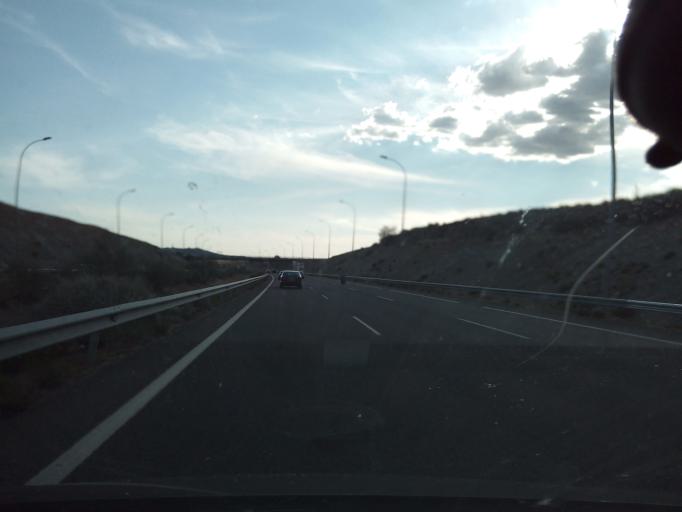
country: ES
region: Madrid
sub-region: Provincia de Madrid
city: Villa de Vallecas
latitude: 40.3350
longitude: -3.6263
